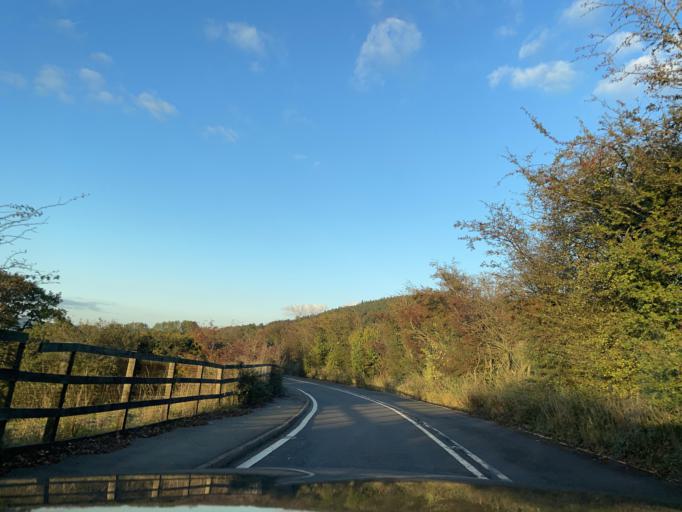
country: GB
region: England
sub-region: Borough of Stockport
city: Marple
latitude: 53.4145
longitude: -2.0347
